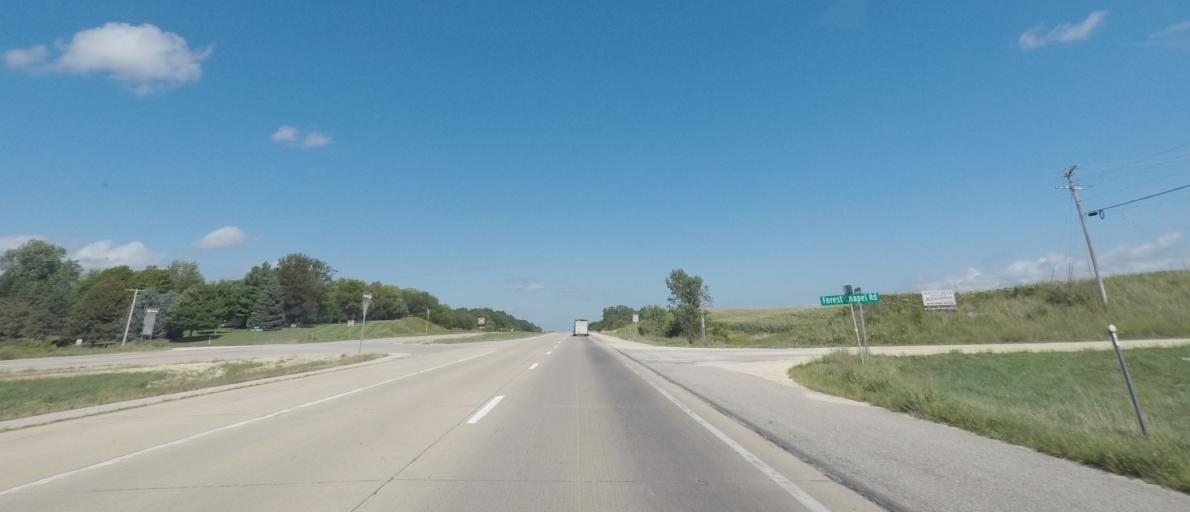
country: US
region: Iowa
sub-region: Jones County
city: Anamosa
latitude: 42.0738
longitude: -91.2877
